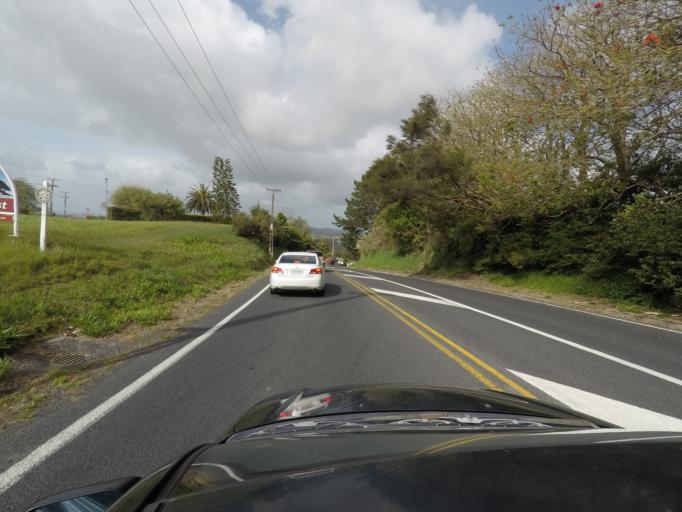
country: NZ
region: Auckland
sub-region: Auckland
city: Pakuranga
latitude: -36.9447
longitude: 174.9546
